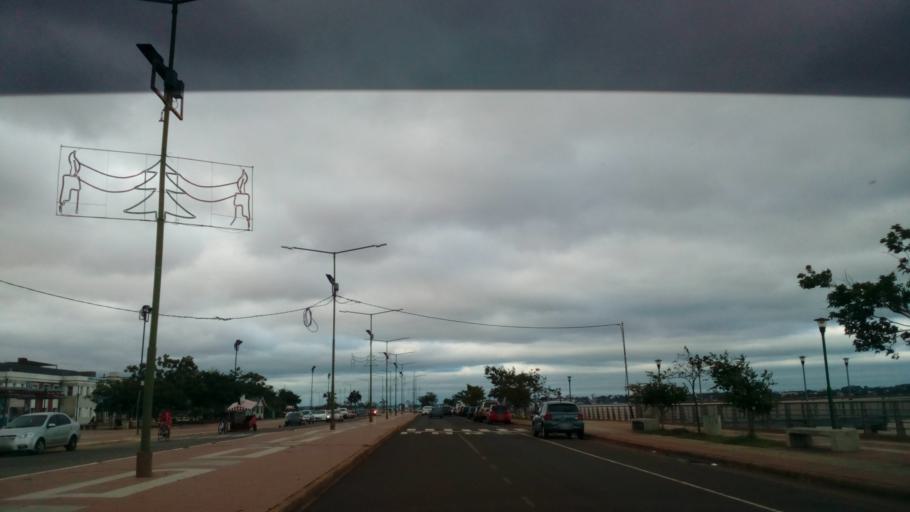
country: AR
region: Misiones
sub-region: Departamento de Capital
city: Posadas
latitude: -27.3706
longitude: -55.8849
